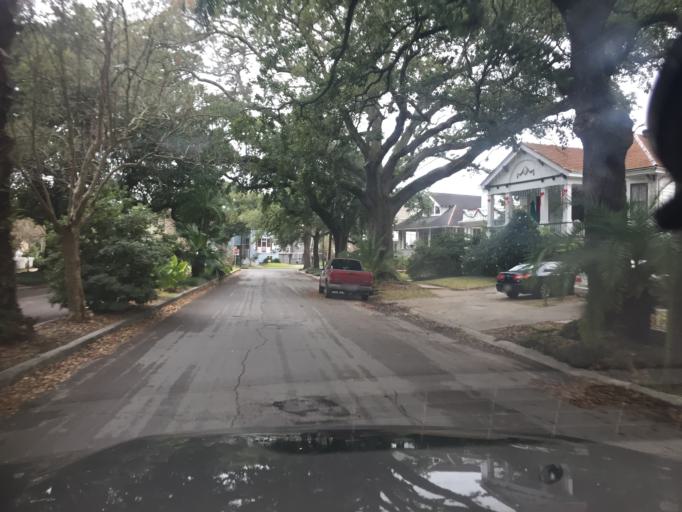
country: US
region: Louisiana
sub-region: Orleans Parish
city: New Orleans
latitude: 29.9778
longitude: -90.0857
